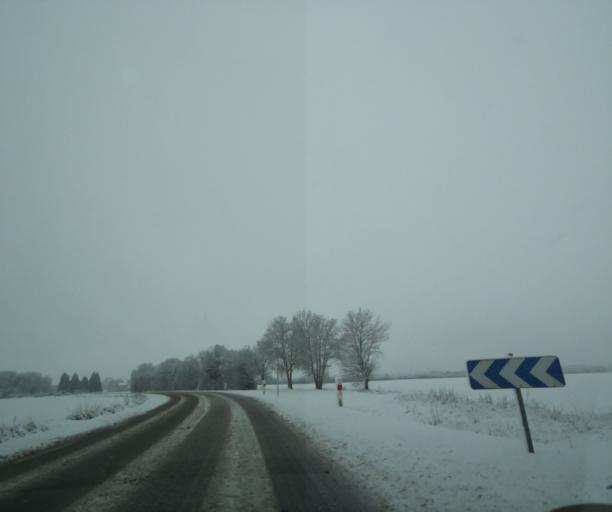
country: FR
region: Champagne-Ardenne
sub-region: Departement de la Haute-Marne
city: Saint-Dizier
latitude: 48.5921
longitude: 4.9026
